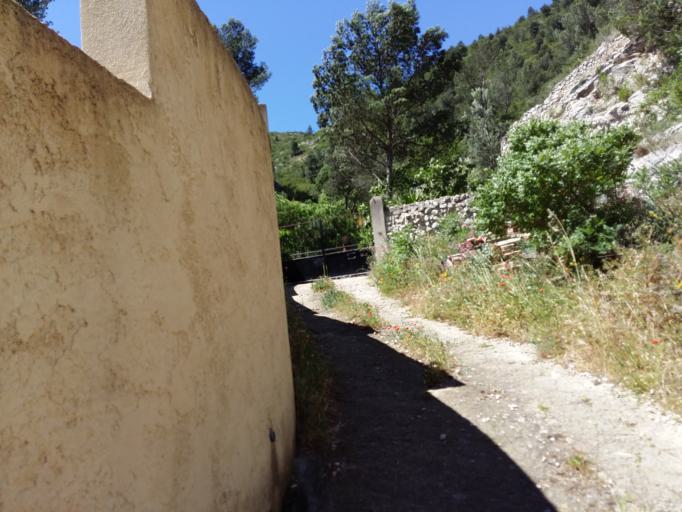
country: FR
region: Provence-Alpes-Cote d'Azur
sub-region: Departement des Bouches-du-Rhone
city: Marseille 11
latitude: 43.2806
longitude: 5.4762
